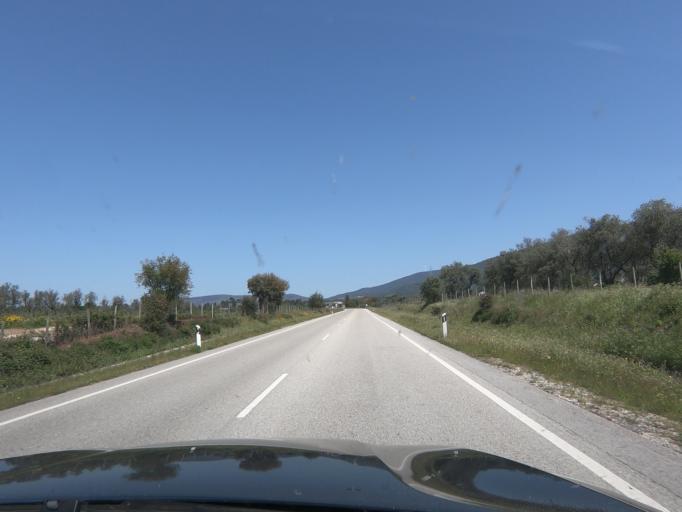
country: PT
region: Coimbra
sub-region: Lousa
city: Lousa
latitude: 40.1285
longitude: -8.2614
